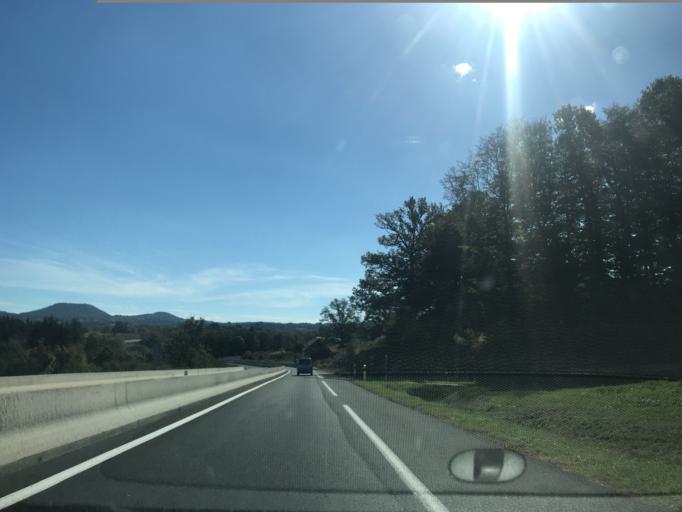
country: FR
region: Auvergne
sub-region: Departement du Puy-de-Dome
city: Gelles
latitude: 45.7378
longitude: 2.8608
